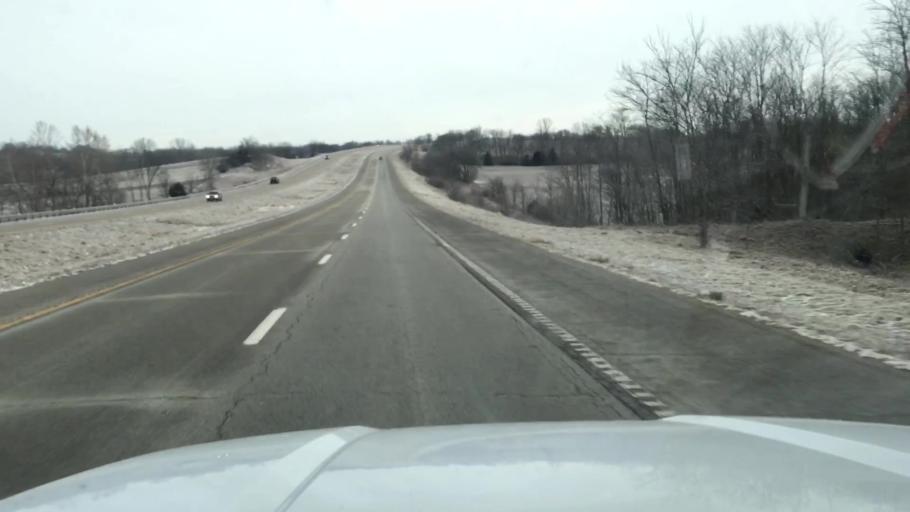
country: US
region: Missouri
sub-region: Andrew County
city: Savannah
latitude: 39.9059
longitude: -94.8583
